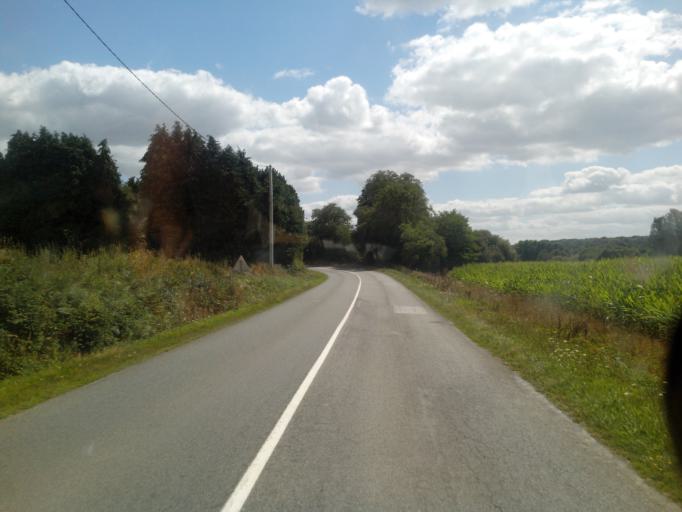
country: FR
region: Brittany
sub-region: Departement des Cotes-d'Armor
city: Plumieux
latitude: 48.0716
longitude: -2.5438
